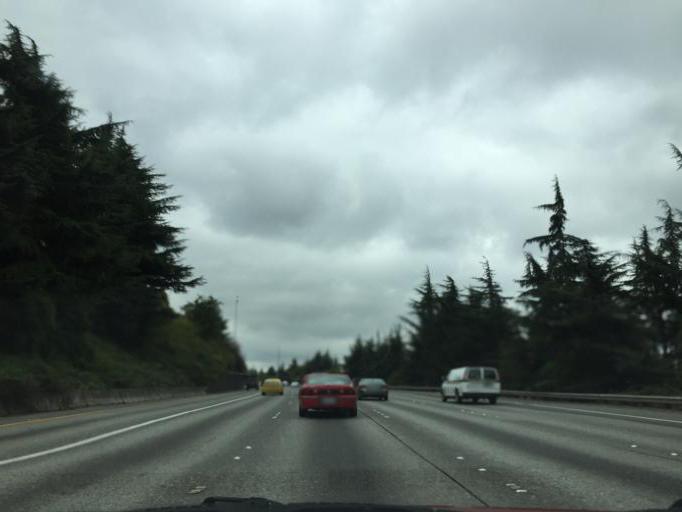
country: US
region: Washington
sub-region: King County
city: Seattle
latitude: 47.5613
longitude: -122.3220
